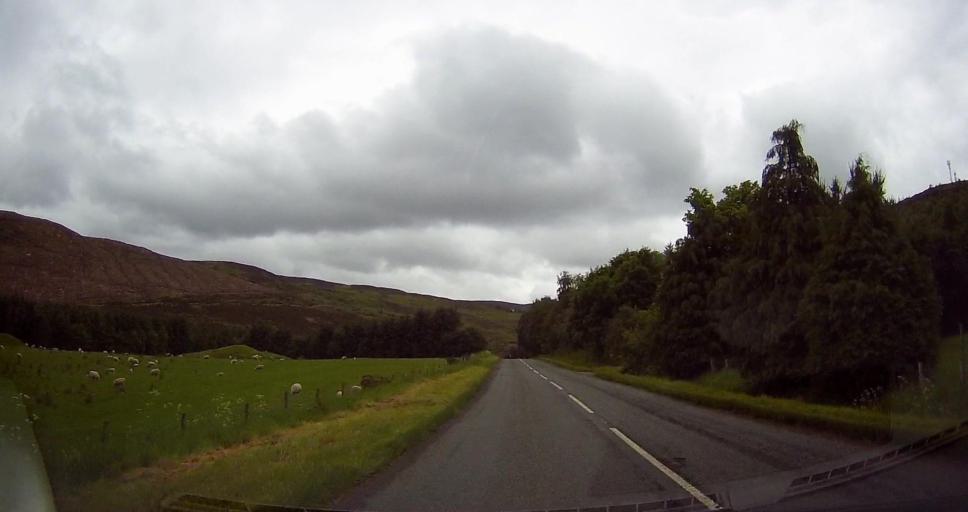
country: GB
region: Scotland
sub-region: Highland
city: Dornoch
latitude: 58.0047
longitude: -4.1843
